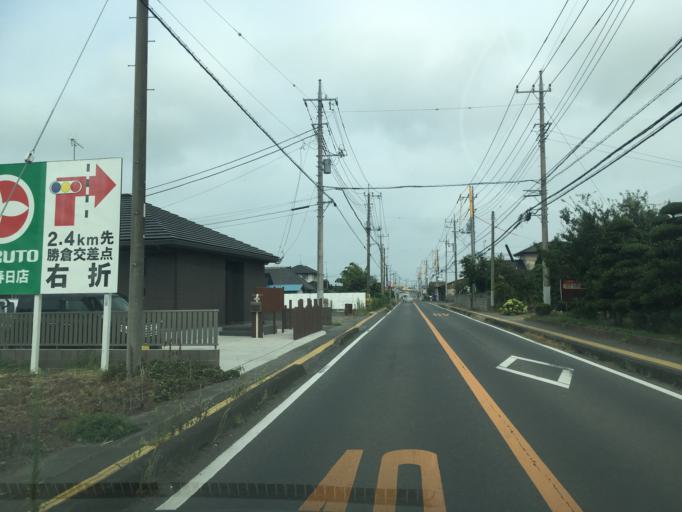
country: JP
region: Ibaraki
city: Katsuta
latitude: 36.3717
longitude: 140.5470
